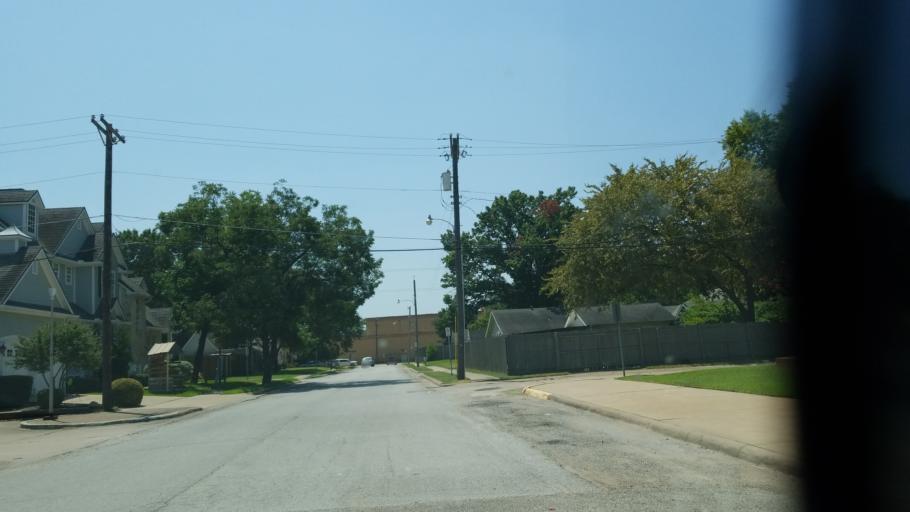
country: US
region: Texas
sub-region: Dallas County
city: Garland
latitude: 32.9124
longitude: -96.6450
